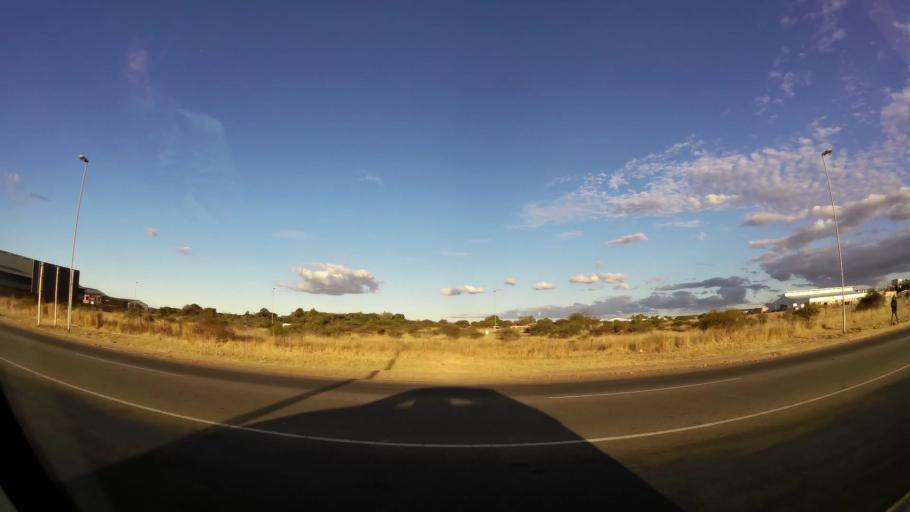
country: ZA
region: Limpopo
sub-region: Capricorn District Municipality
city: Polokwane
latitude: -23.8589
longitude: 29.4723
